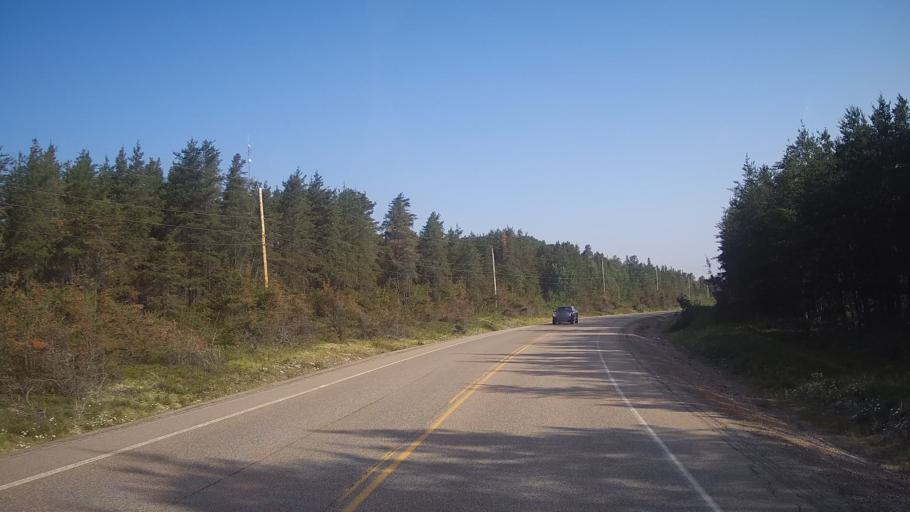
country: CA
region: Ontario
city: Rayside-Balfour
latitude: 46.7079
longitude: -81.5613
